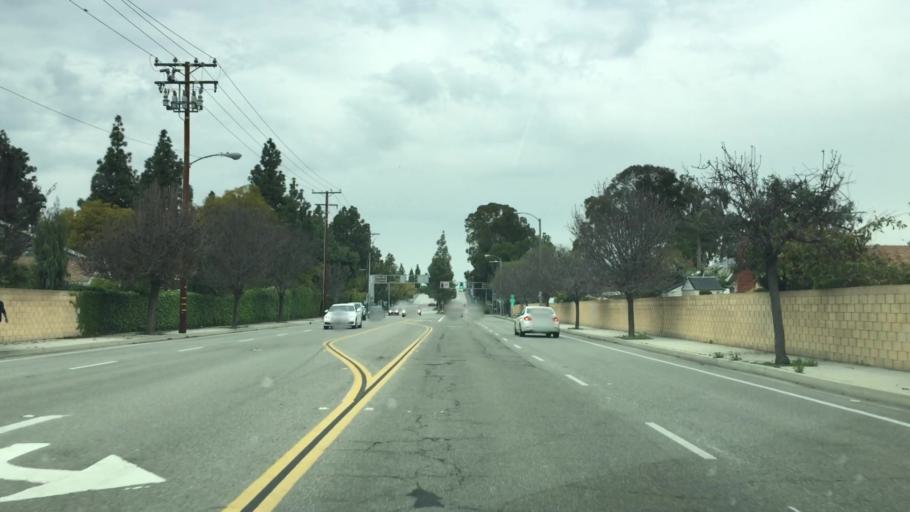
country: US
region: California
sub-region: Los Angeles County
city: Cerritos
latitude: 33.8644
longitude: -118.0550
